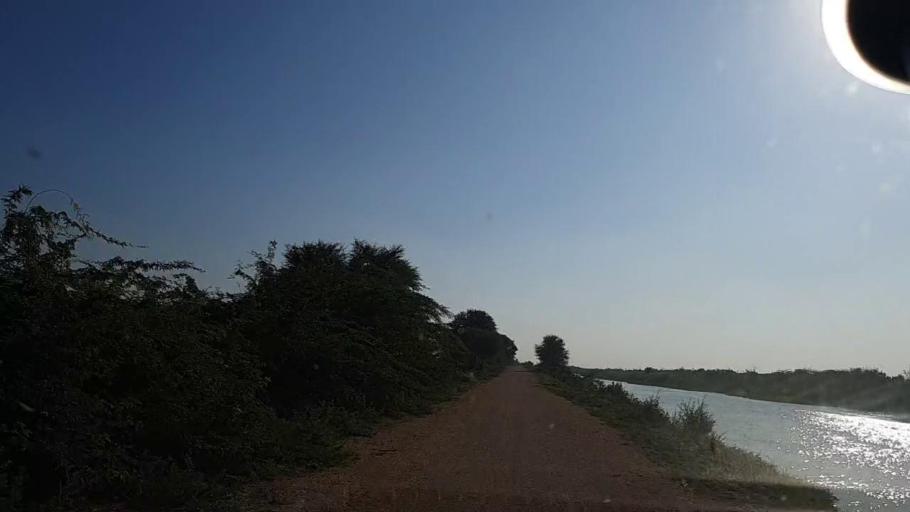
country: PK
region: Sindh
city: Chuhar Jamali
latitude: 24.5555
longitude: 68.0374
